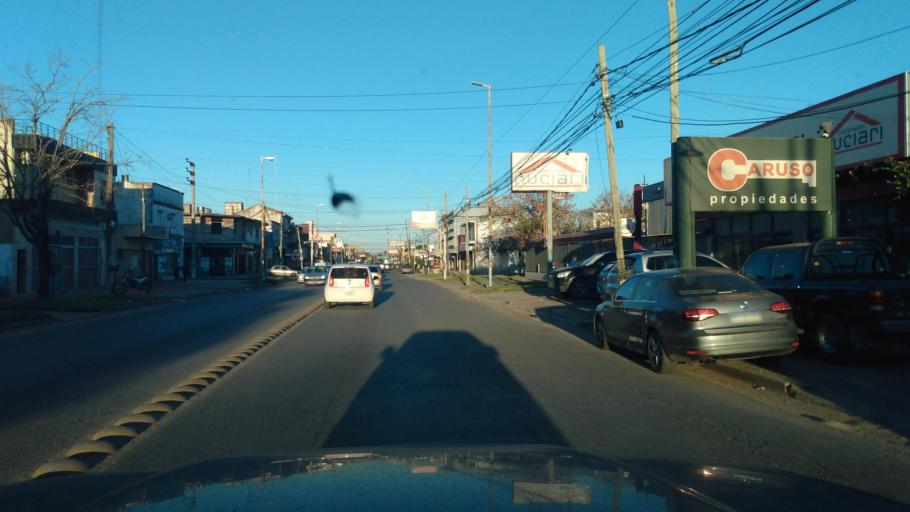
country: AR
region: Buenos Aires
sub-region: Partido de Merlo
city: Merlo
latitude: -34.6562
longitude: -58.7646
